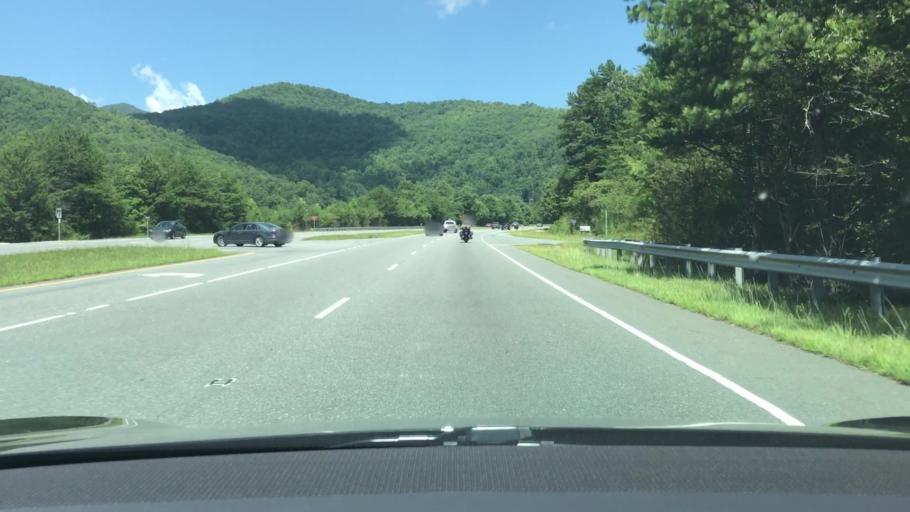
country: US
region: North Carolina
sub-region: Jackson County
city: Sylva
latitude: 35.3413
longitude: -83.2541
